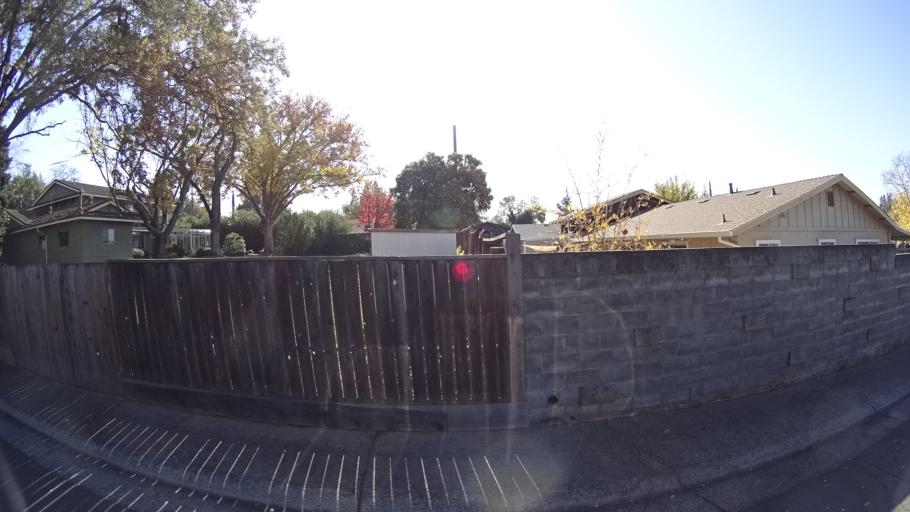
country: US
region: California
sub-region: Sacramento County
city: Citrus Heights
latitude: 38.6947
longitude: -121.2819
